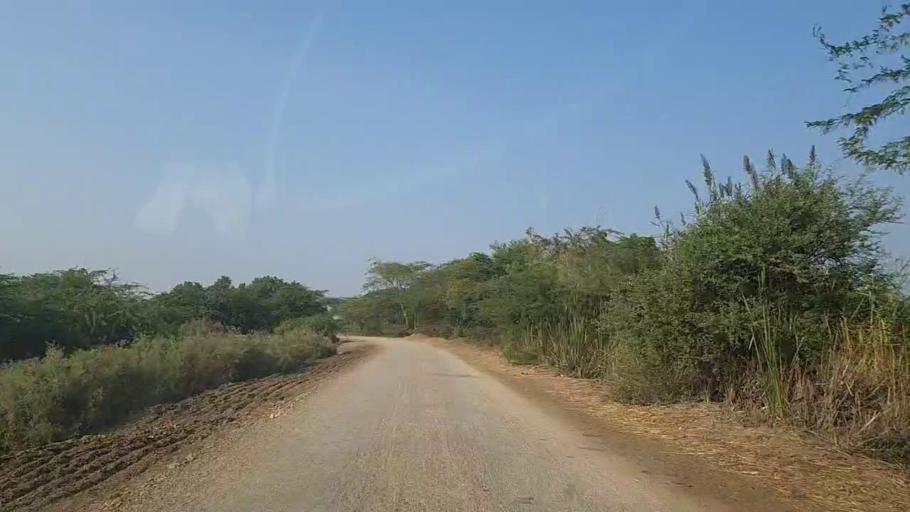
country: PK
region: Sindh
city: Mirpur Sakro
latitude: 24.5719
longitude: 67.6662
